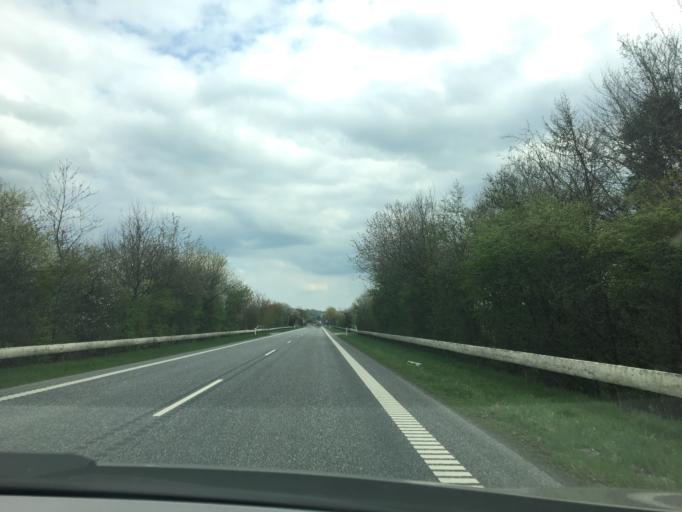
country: DK
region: Central Jutland
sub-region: Horsens Kommune
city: Braedstrup
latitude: 55.9474
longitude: 9.6393
